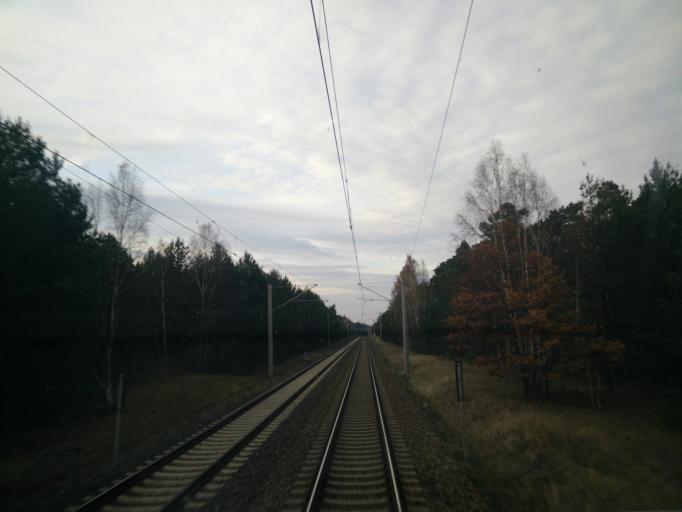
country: DE
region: Brandenburg
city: Gross Koris
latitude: 52.1422
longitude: 13.6660
